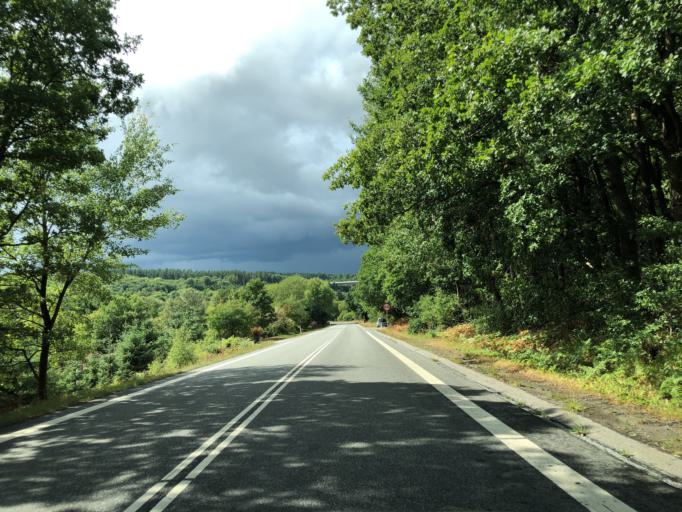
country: DK
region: Central Jutland
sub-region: Silkeborg Kommune
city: Silkeborg
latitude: 56.1403
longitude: 9.4185
